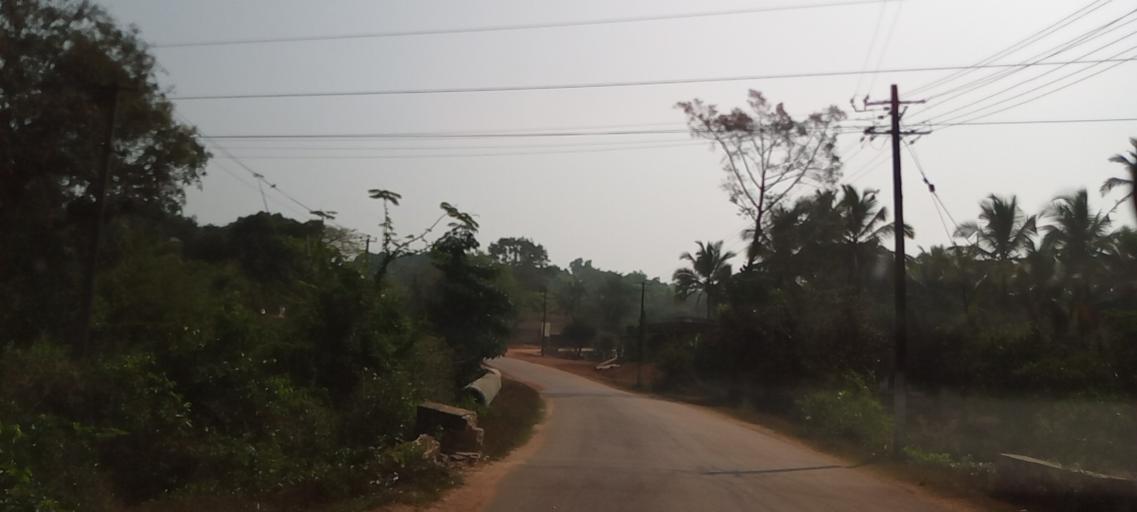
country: IN
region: Karnataka
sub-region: Udupi
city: Manipala
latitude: 13.5126
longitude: 74.8400
